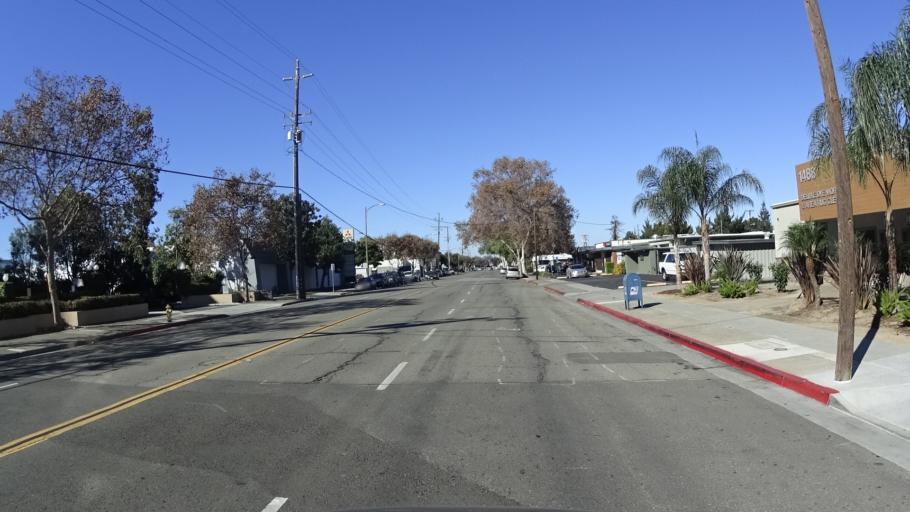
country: US
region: California
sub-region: Santa Clara County
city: San Jose
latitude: 37.3650
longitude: -121.9077
